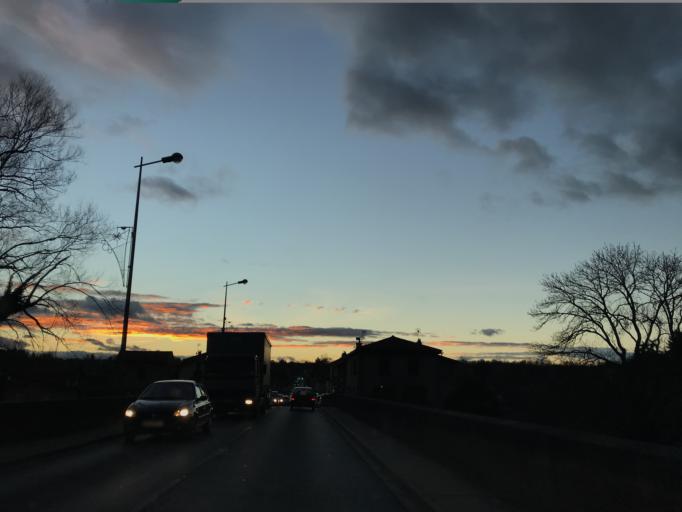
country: FR
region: Auvergne
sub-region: Departement du Puy-de-Dome
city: Peschadoires
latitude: 45.8392
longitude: 3.5007
